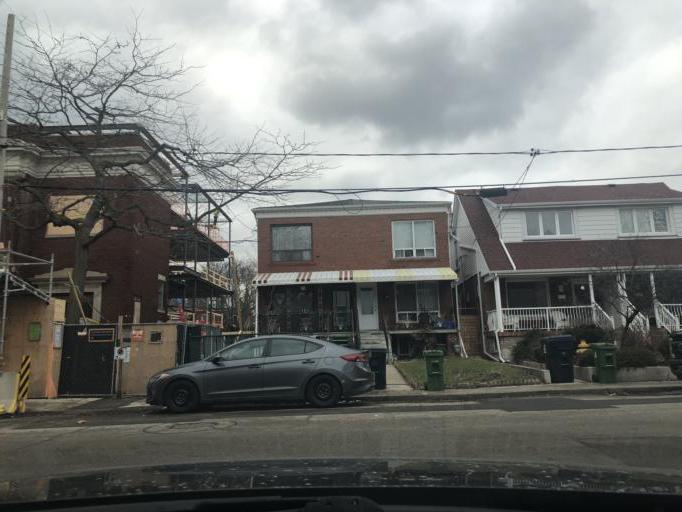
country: CA
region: Ontario
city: Toronto
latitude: 43.6809
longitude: -79.3396
